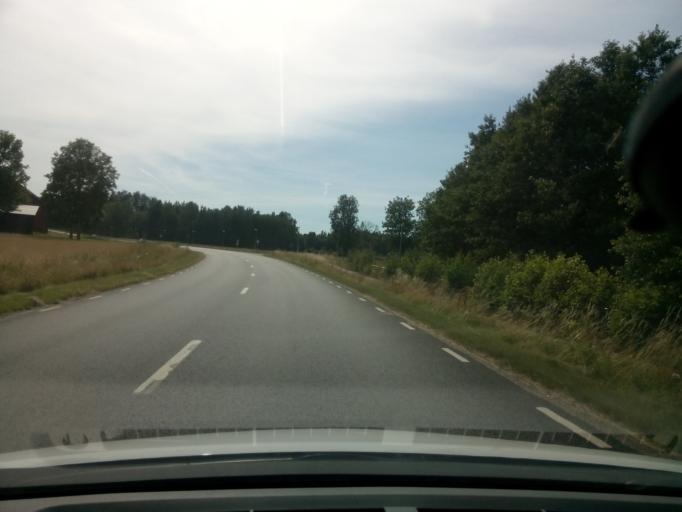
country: SE
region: Soedermanland
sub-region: Nykopings Kommun
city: Nykoping
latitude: 58.7751
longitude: 17.0730
